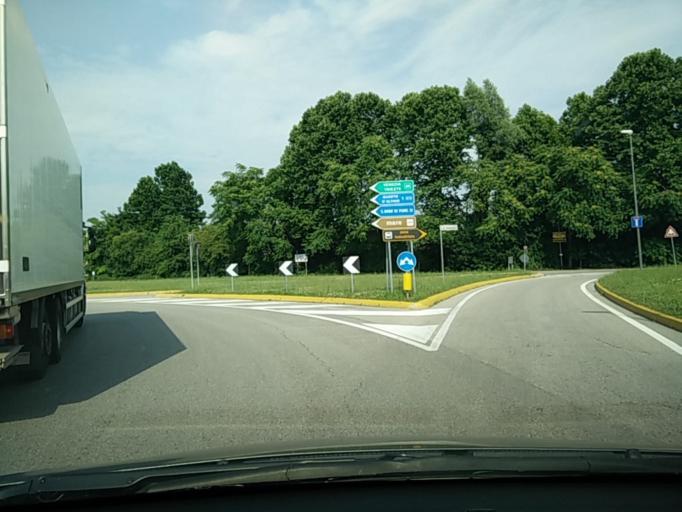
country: IT
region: Veneto
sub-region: Provincia di Treviso
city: Casale sul Sile
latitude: 45.5862
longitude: 12.3431
